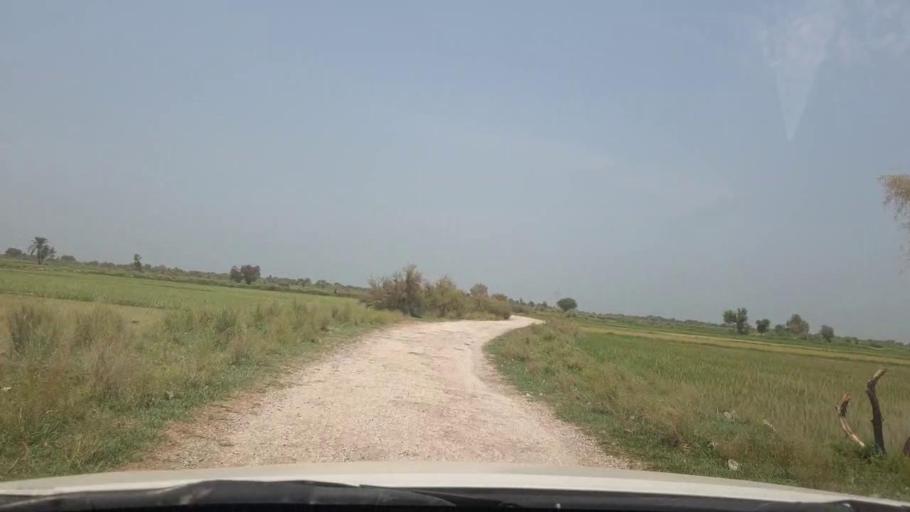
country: PK
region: Sindh
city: Rustam jo Goth
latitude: 28.0503
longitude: 68.7511
